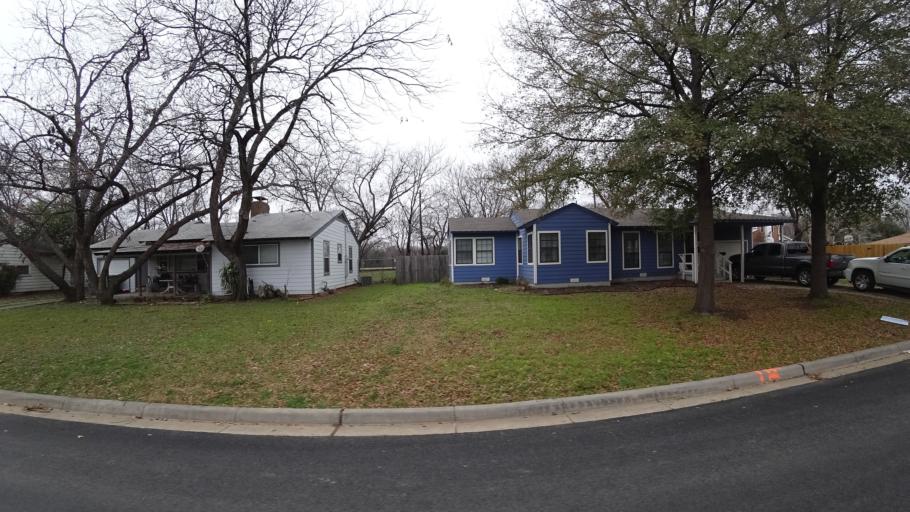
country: US
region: Texas
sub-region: Denton County
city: Lewisville
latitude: 33.0514
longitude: -97.0037
